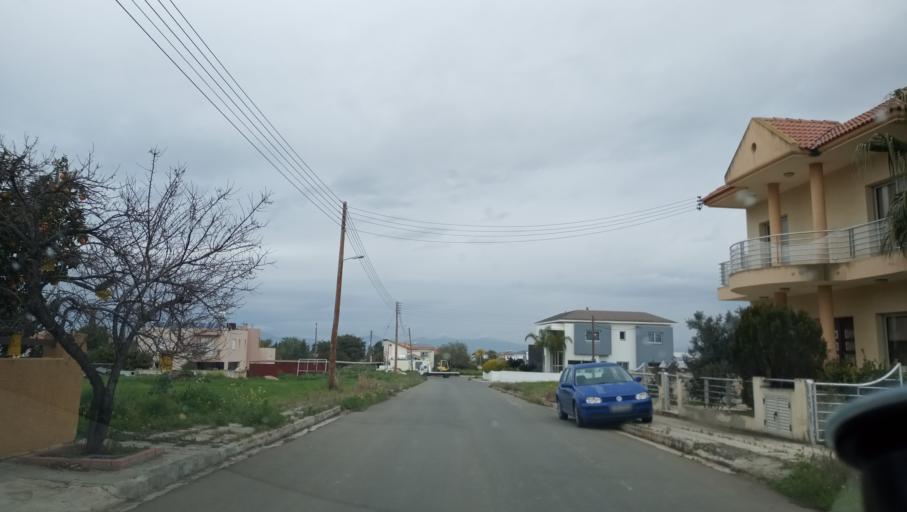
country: CY
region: Lefkosia
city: Kato Deftera
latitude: 35.0838
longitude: 33.2872
